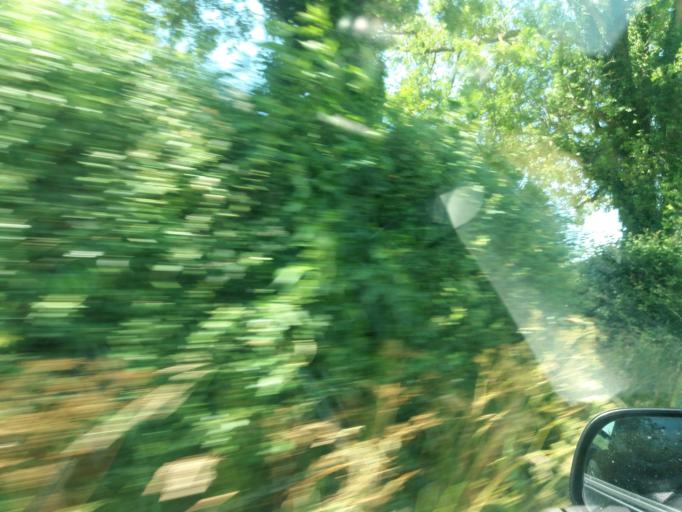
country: IE
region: Leinster
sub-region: Fingal County
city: Swords
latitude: 53.5218
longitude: -6.2357
